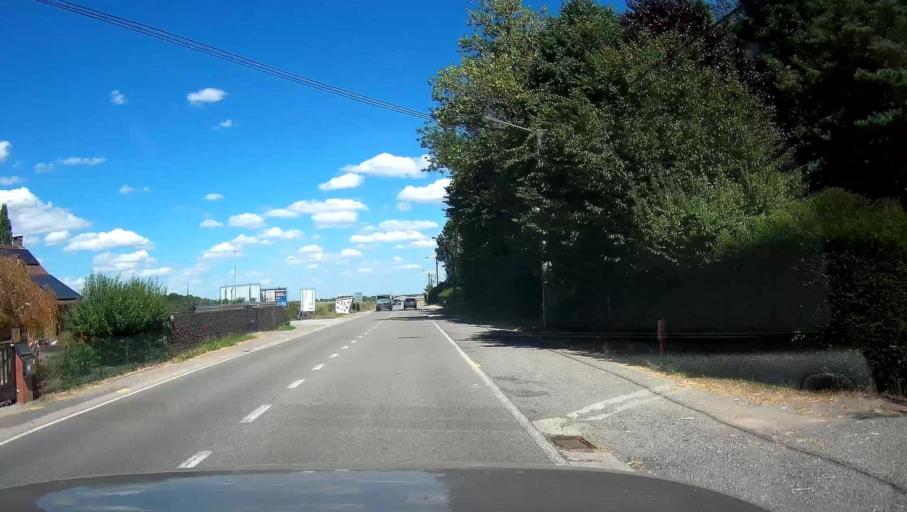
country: BE
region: Wallonia
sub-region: Province du Hainaut
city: Gerpinnes
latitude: 50.3443
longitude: 4.4783
